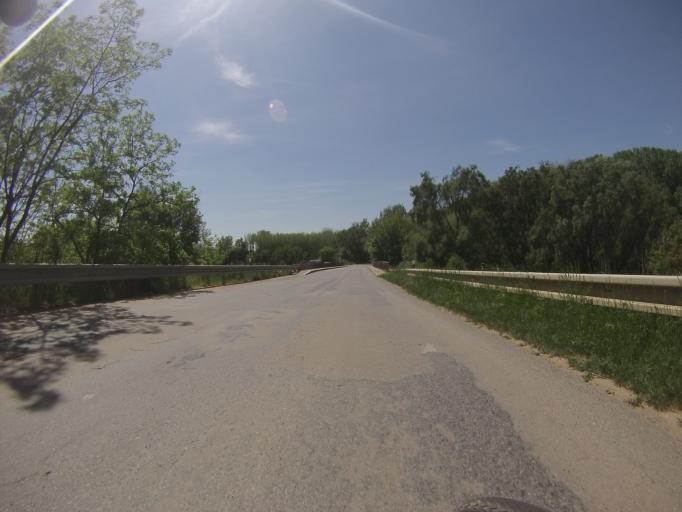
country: CZ
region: South Moravian
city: Vranovice
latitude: 48.9283
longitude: 16.5731
